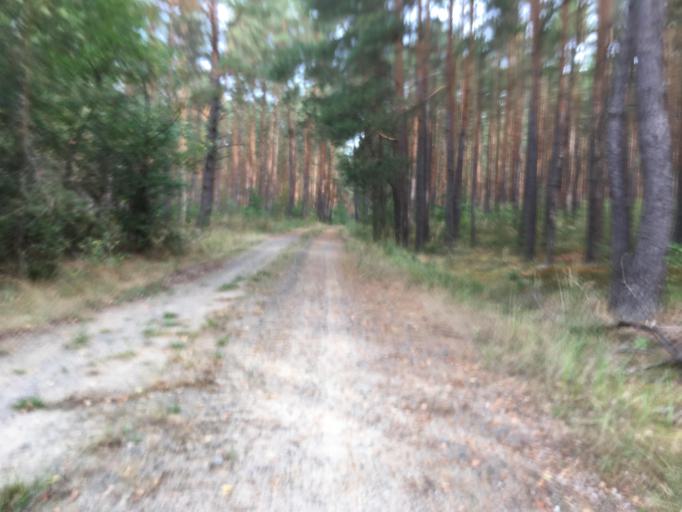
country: DE
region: Brandenburg
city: Friedrichswalde
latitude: 53.0129
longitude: 13.6053
